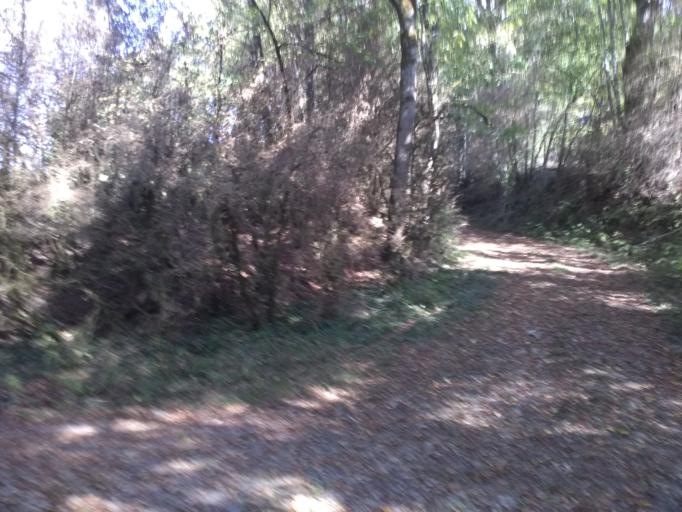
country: FR
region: Midi-Pyrenees
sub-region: Departement de l'Aveyron
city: Bozouls
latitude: 44.4786
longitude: 2.6732
